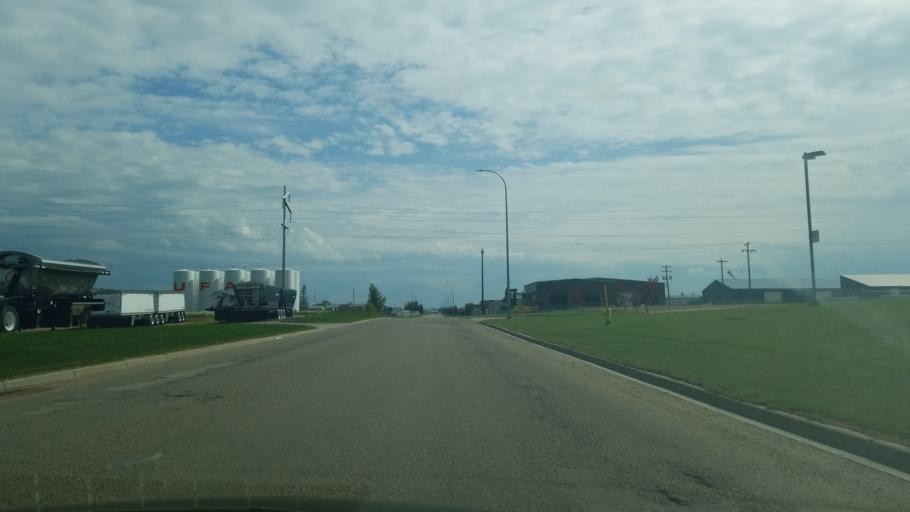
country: CA
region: Saskatchewan
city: Lloydminster
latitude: 53.2935
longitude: -110.0367
